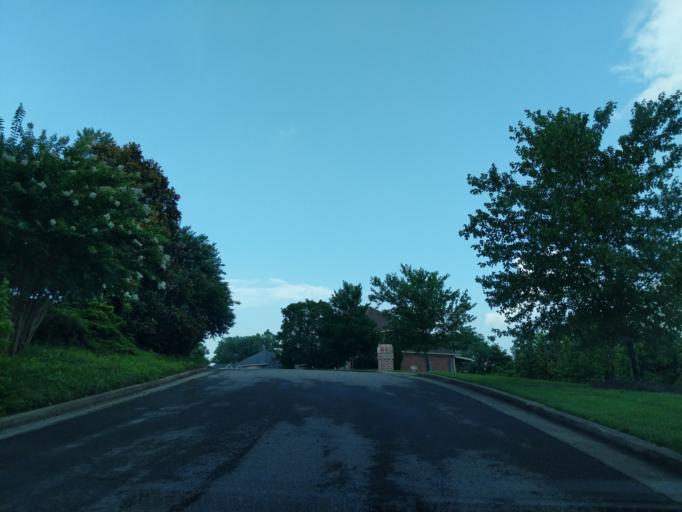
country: US
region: Tennessee
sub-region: Davidson County
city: Belle Meade
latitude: 36.0417
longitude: -86.9462
